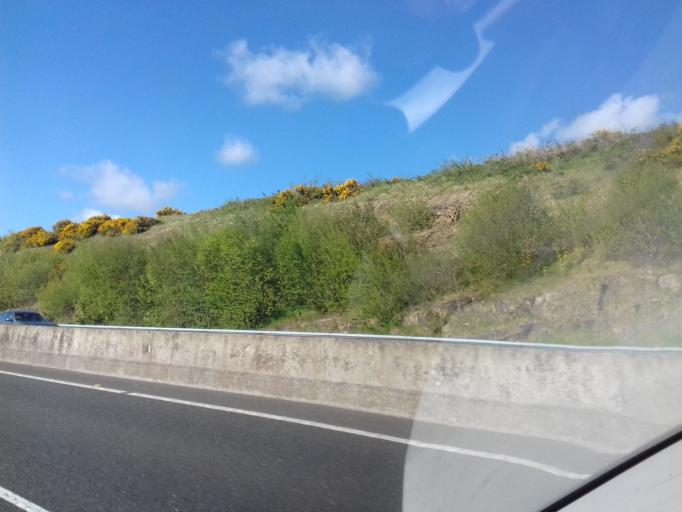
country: IE
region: Munster
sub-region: Waterford
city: Waterford
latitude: 52.3421
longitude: -7.1643
